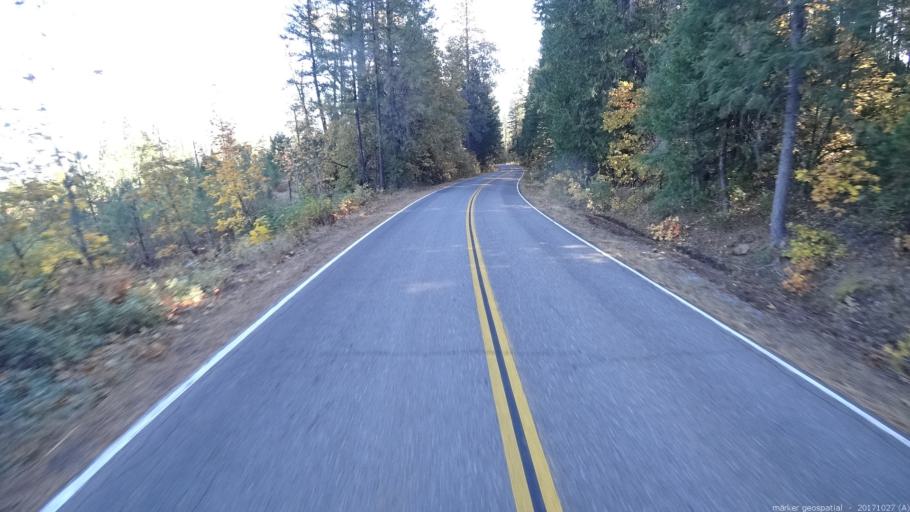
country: US
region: California
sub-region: Shasta County
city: Burney
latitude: 41.0015
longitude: -121.9165
